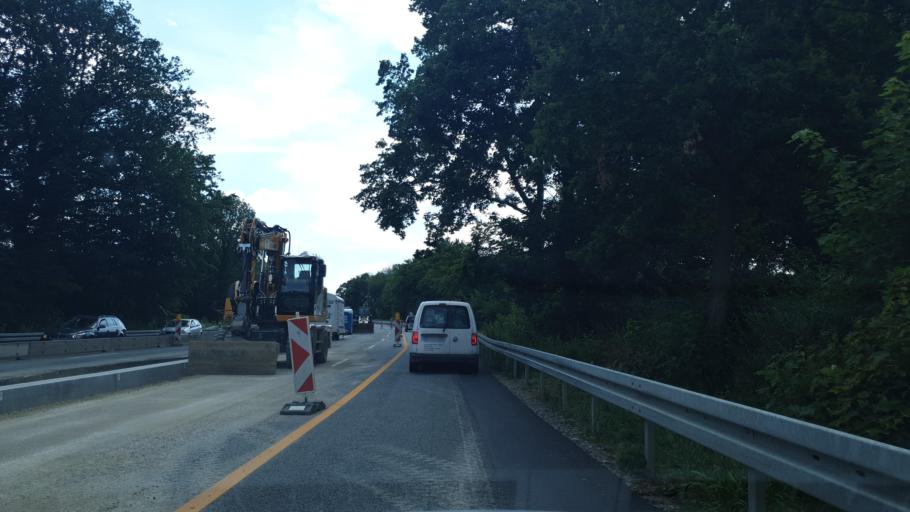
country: DE
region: North Rhine-Westphalia
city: Loehne
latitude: 52.1834
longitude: 8.7483
